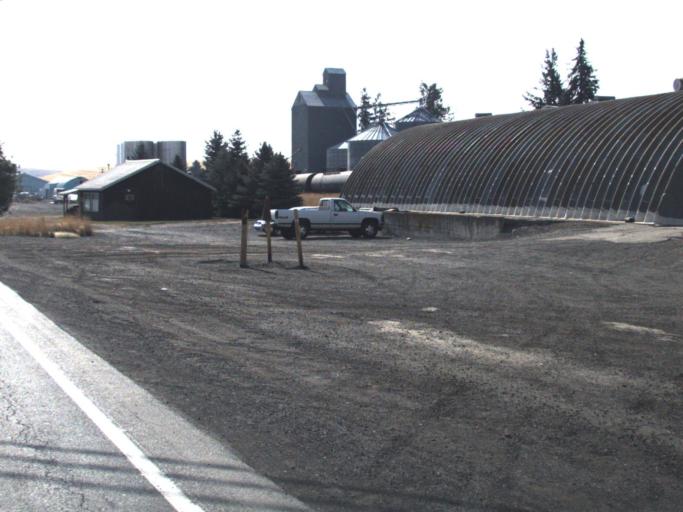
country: US
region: Washington
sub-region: Whitman County
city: Colfax
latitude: 47.1257
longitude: -117.2375
